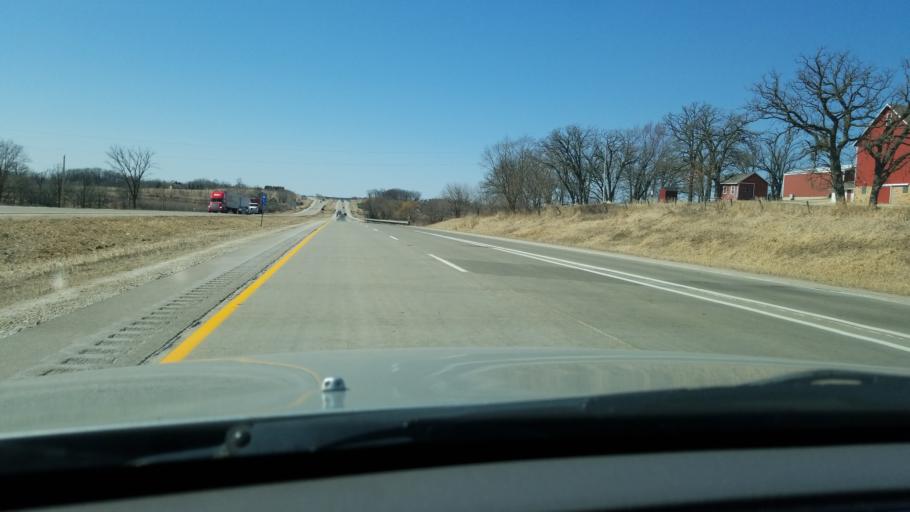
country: US
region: Wisconsin
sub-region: Dane County
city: Verona
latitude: 42.9868
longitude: -89.5654
